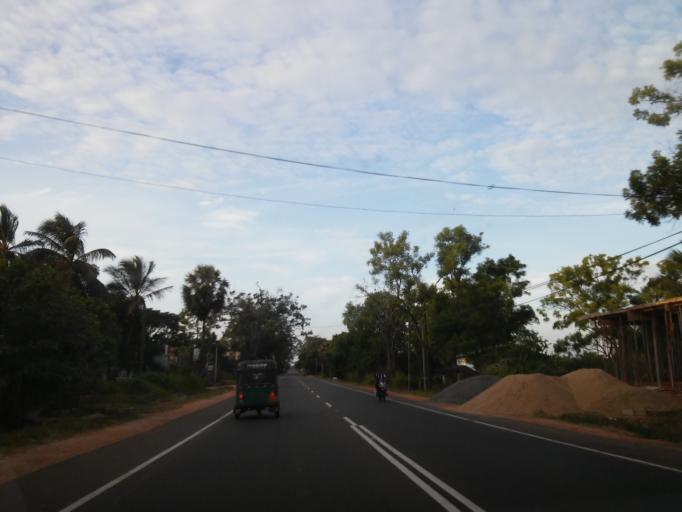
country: LK
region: North Central
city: Anuradhapura
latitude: 8.2161
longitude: 80.5229
